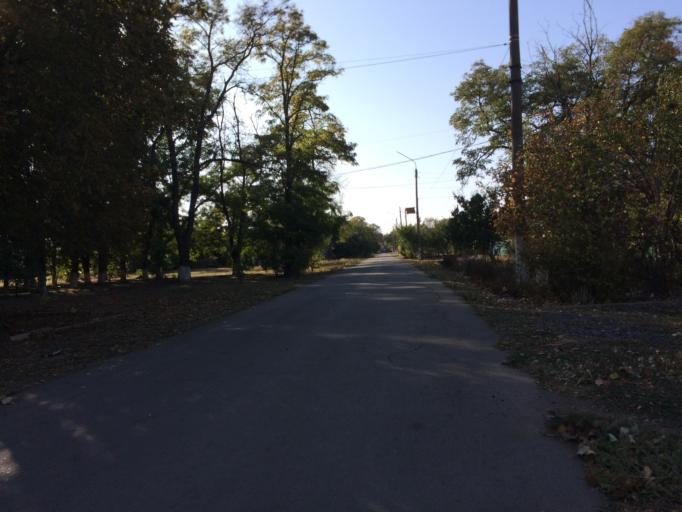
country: RU
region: Rostov
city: Gigant
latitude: 46.5160
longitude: 41.1877
